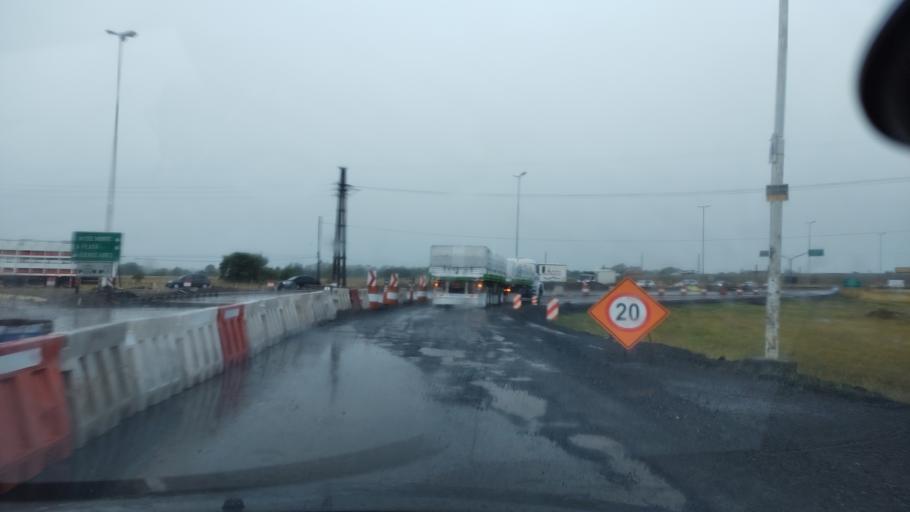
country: AR
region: Buenos Aires
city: Canuelas
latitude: -35.0205
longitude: -58.7466
